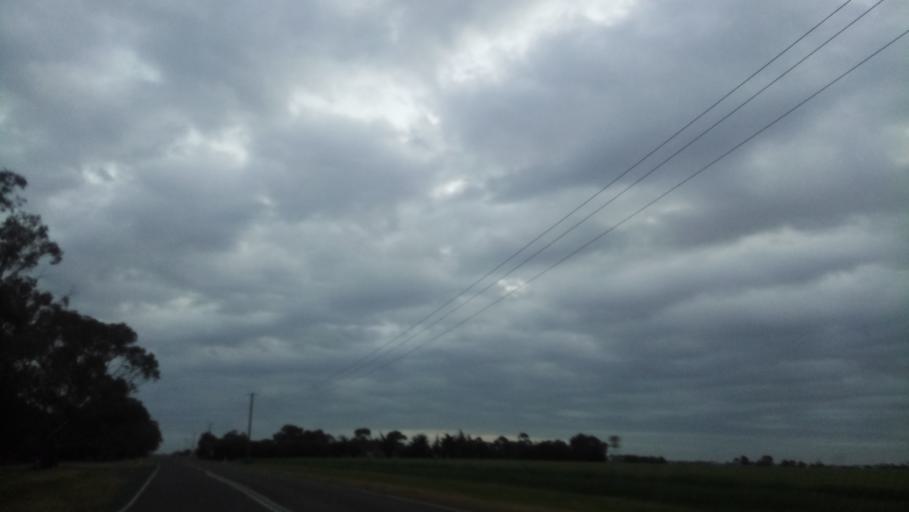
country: AU
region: Victoria
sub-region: Wyndham
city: Point Cook
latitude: -37.9240
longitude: 144.7439
